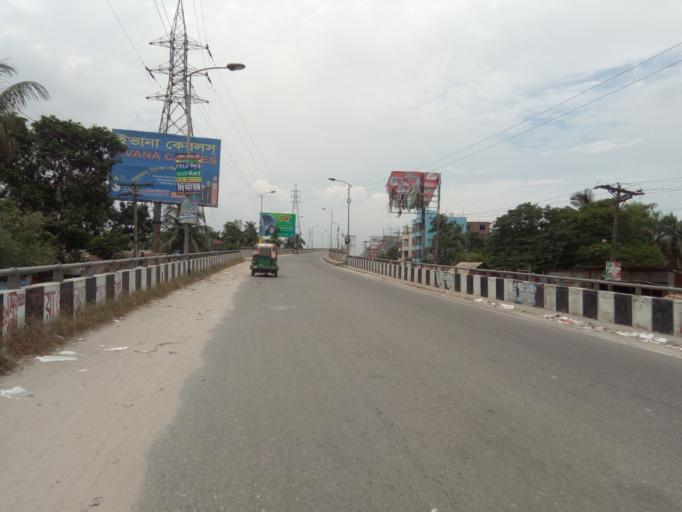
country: BD
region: Dhaka
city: Paltan
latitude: 23.7222
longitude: 90.5061
